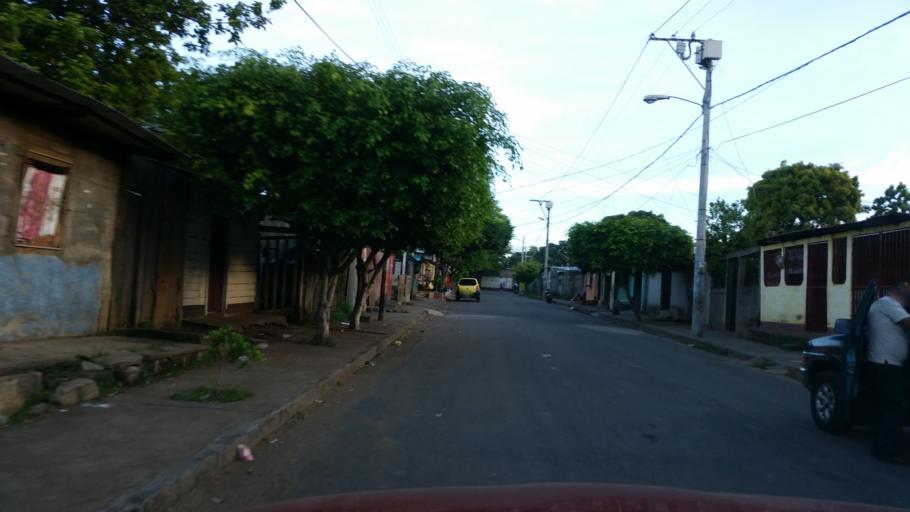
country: NI
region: Managua
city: Managua
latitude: 12.1282
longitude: -86.2886
